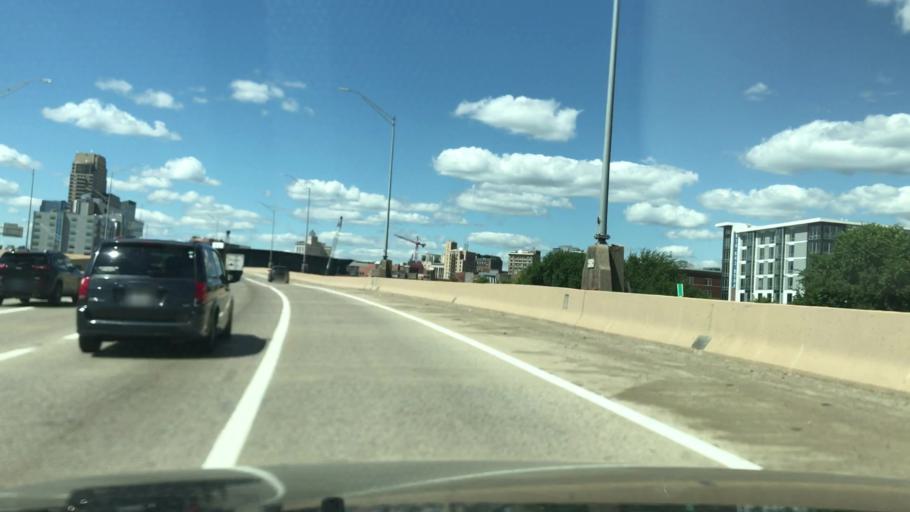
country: US
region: Michigan
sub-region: Kent County
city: Grand Rapids
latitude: 42.9571
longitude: -85.6711
